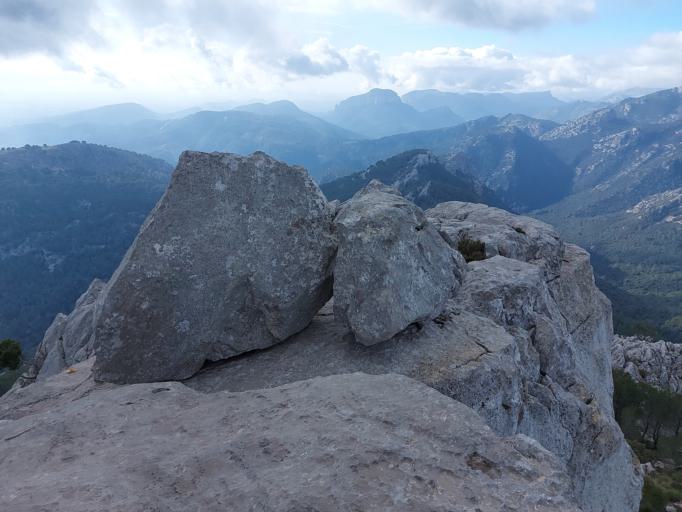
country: ES
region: Balearic Islands
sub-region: Illes Balears
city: Escorca
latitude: 39.7981
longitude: 2.8740
